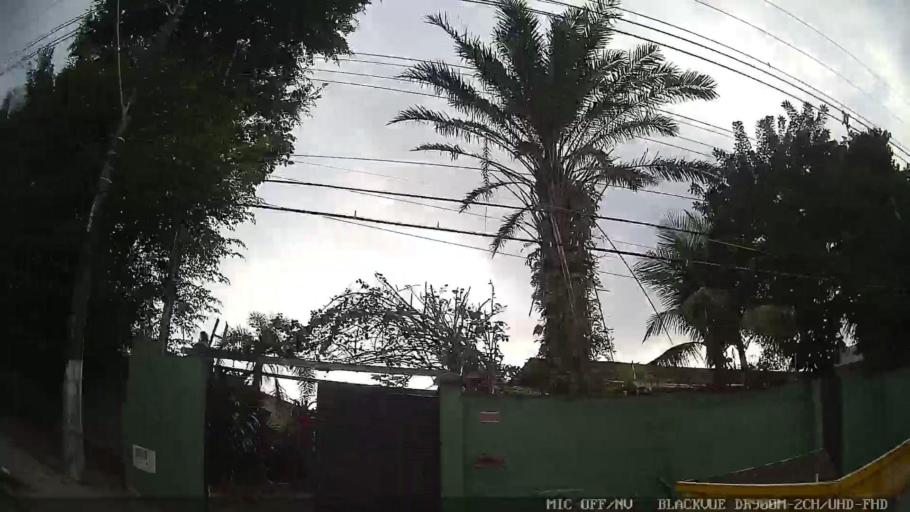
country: BR
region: Sao Paulo
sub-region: Guaruja
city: Guaruja
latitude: -23.9773
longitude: -46.2097
